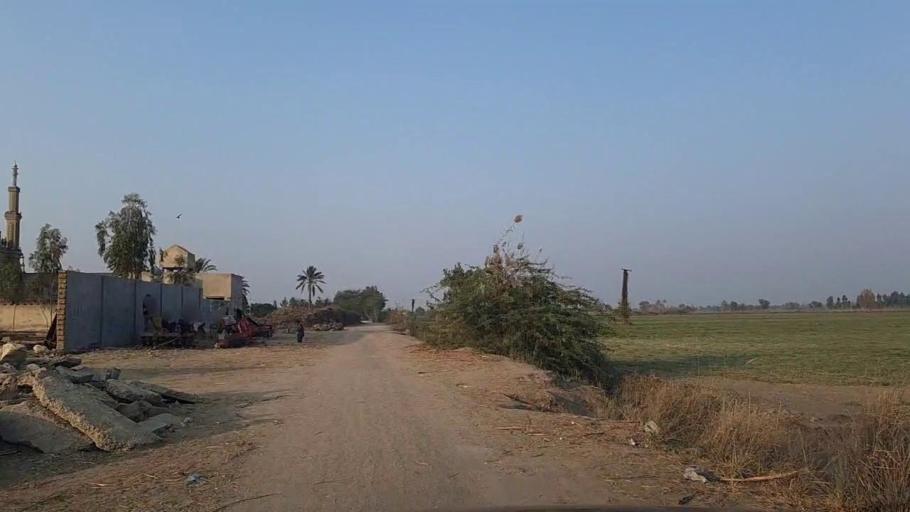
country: PK
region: Sindh
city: Daur
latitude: 26.4241
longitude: 68.3936
